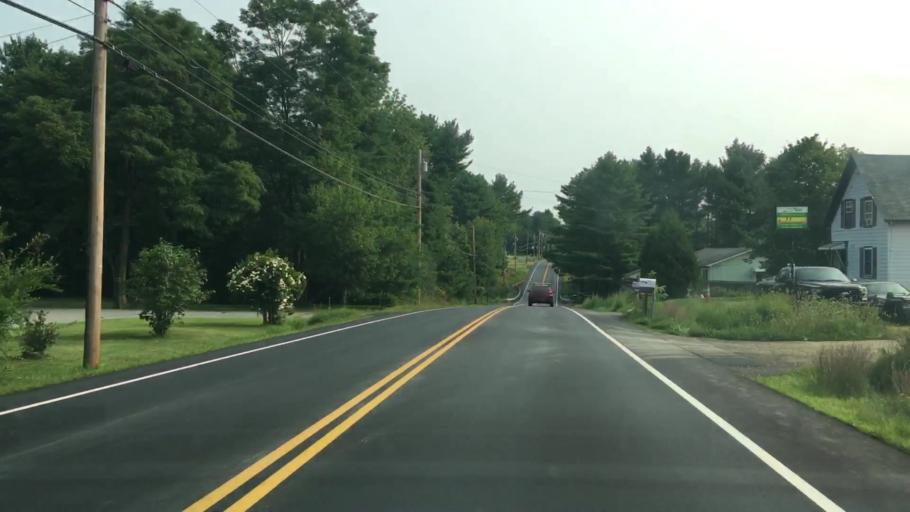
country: US
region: Maine
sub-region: Kennebec County
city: Chelsea
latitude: 44.2653
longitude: -69.7012
